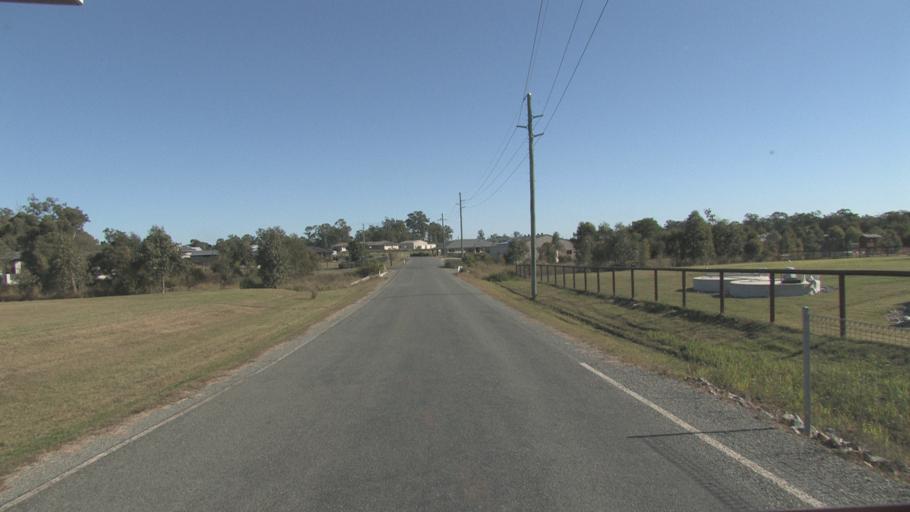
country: AU
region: Queensland
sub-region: Logan
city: Logan Reserve
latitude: -27.7489
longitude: 153.1370
